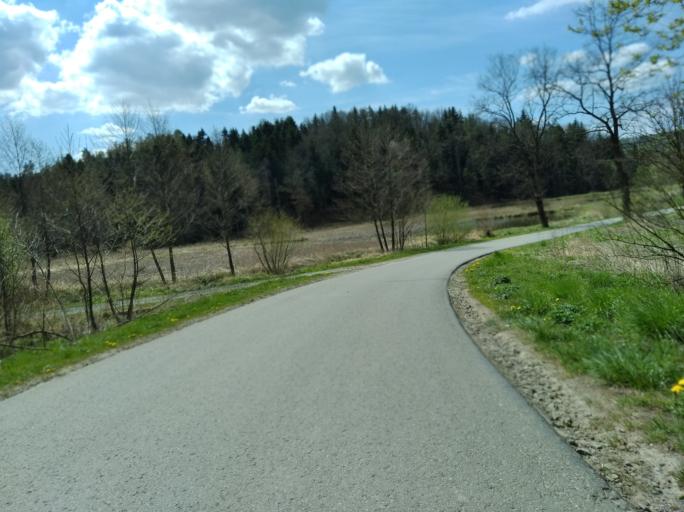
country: PL
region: Subcarpathian Voivodeship
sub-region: Powiat brzozowski
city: Wesola
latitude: 49.7556
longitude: 22.1230
